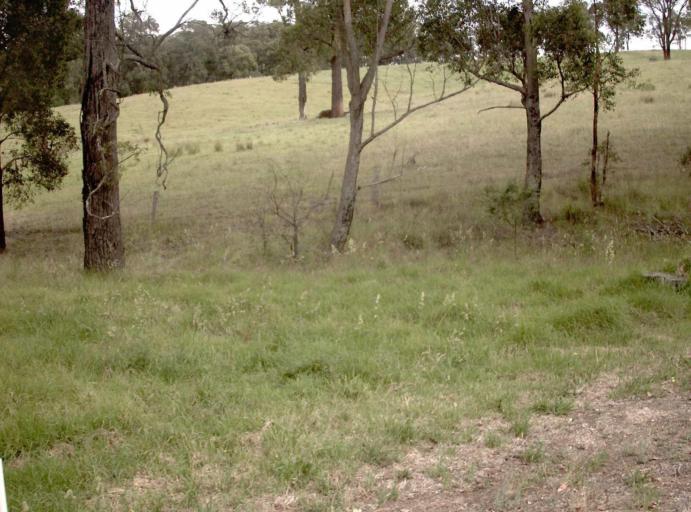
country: AU
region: Victoria
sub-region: East Gippsland
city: Bairnsdale
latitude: -37.7215
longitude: 147.5912
